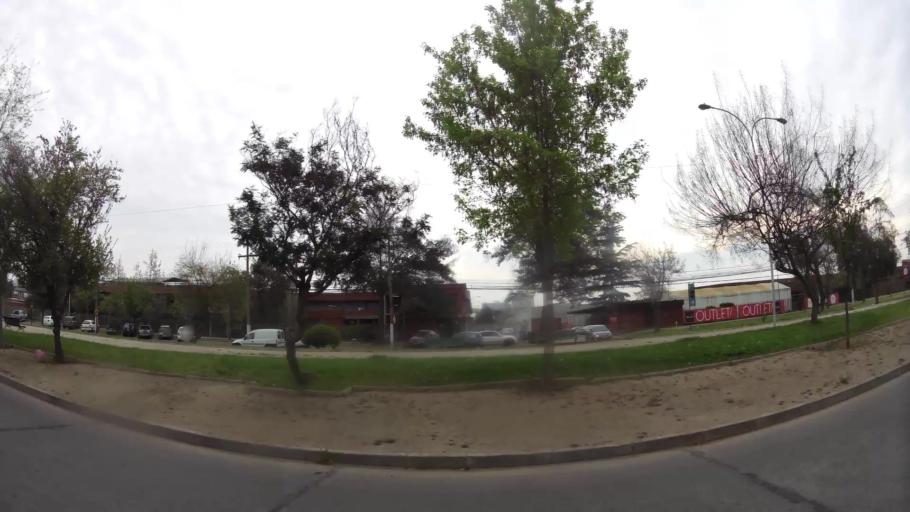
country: CL
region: Santiago Metropolitan
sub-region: Provincia de Santiago
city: Villa Presidente Frei, Nunoa, Santiago, Chile
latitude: -33.4774
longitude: -70.6133
